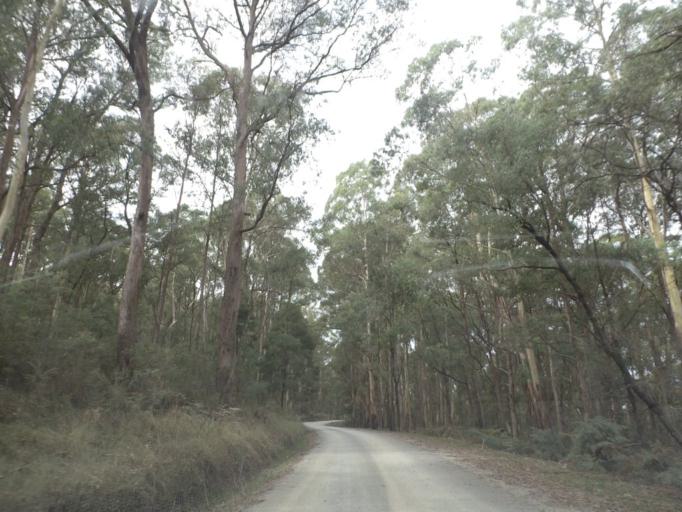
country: AU
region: Victoria
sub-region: Murrindindi
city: Alexandra
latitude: -37.4816
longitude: 145.9747
